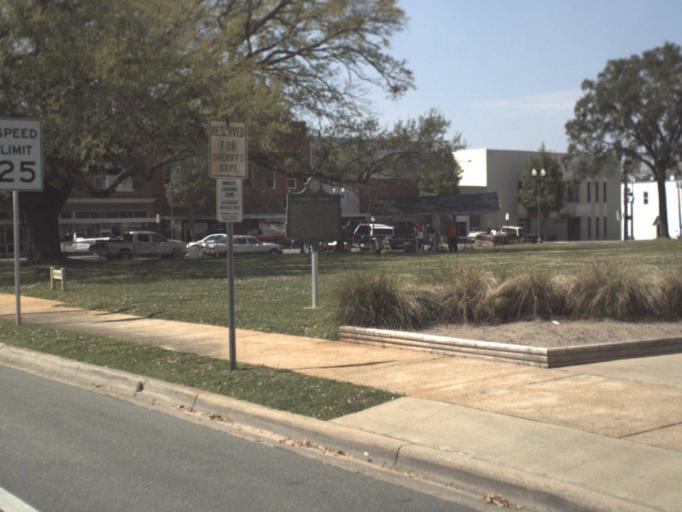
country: US
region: Florida
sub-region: Gadsden County
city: Quincy
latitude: 30.5882
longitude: -84.5763
